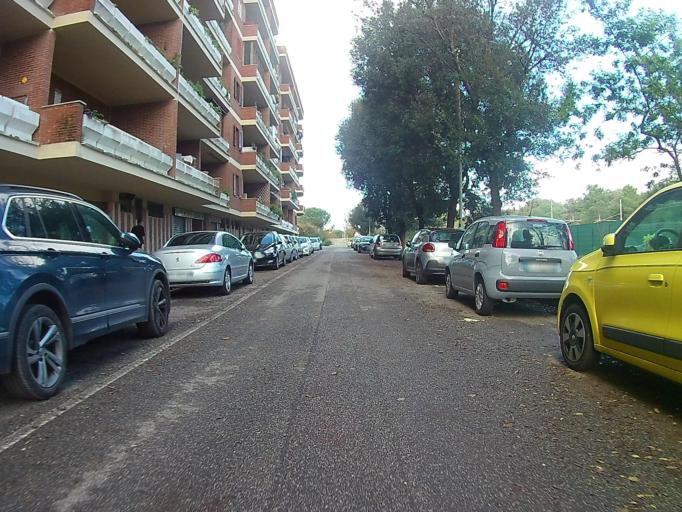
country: IT
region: Latium
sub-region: Citta metropolitana di Roma Capitale
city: Lido di Ostia
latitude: 41.7206
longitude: 12.3080
